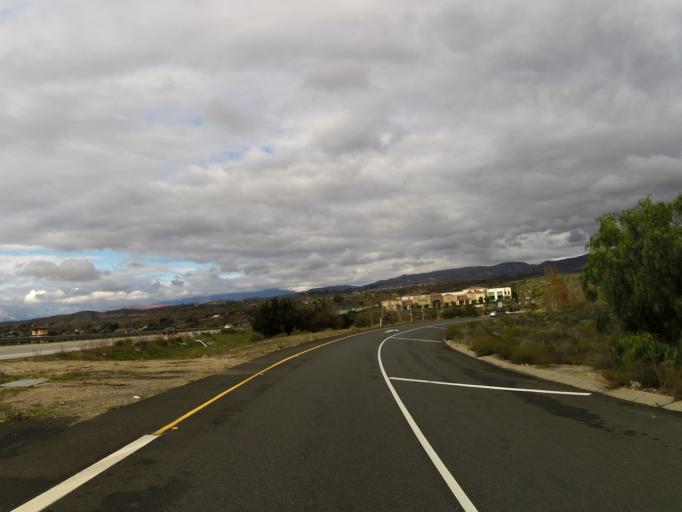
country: US
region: California
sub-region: Ventura County
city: Moorpark
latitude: 34.2800
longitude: -118.8616
